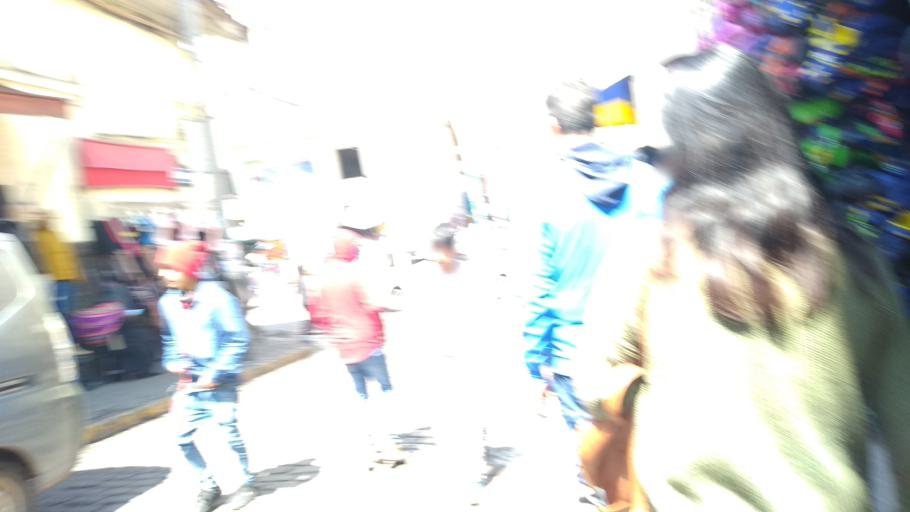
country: PE
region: Cusco
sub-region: Provincia de Cusco
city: Cusco
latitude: -13.5228
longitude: -71.9808
